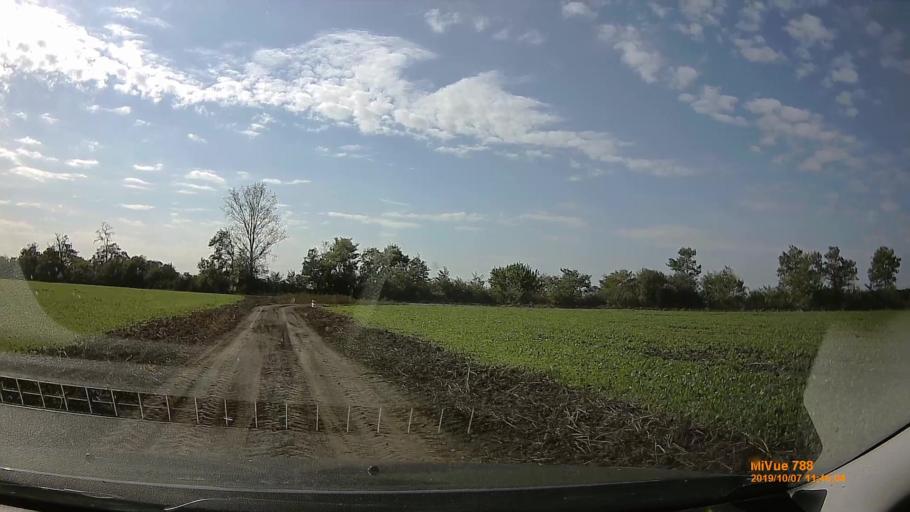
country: HU
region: Bekes
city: Nagyszenas
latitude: 46.8075
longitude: 20.6773
